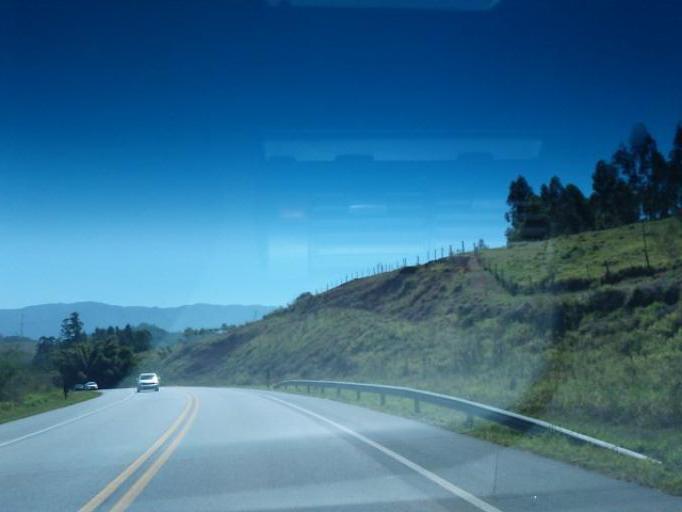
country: BR
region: Sao Paulo
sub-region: Tremembe
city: Tremembe
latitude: -22.9086
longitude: -45.5863
